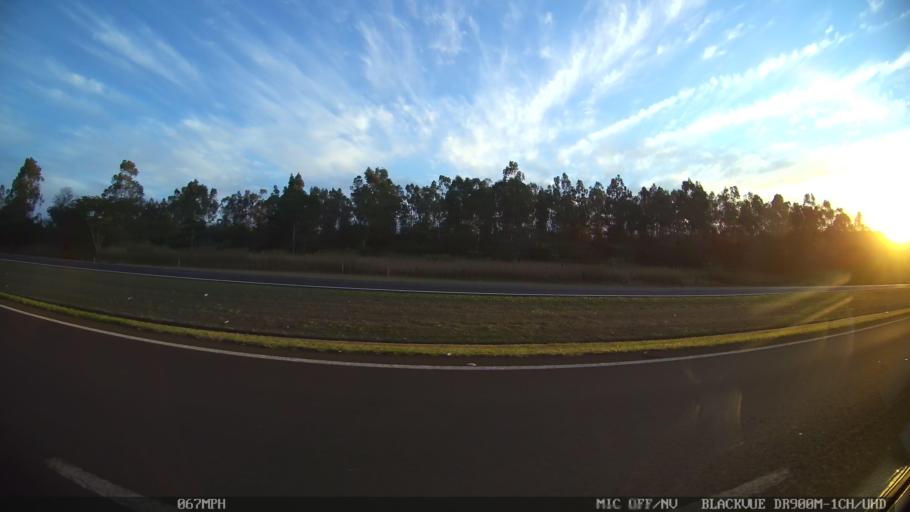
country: BR
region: Sao Paulo
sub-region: Pindorama
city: Pindorama
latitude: -21.2227
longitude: -48.9170
